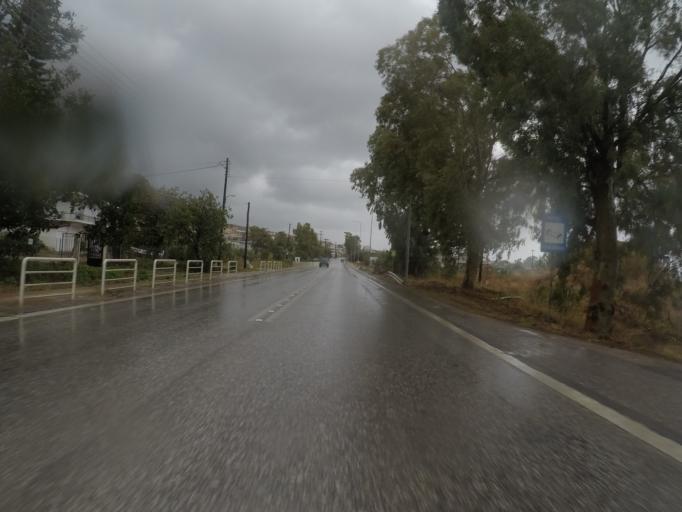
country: GR
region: Peloponnese
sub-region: Nomos Messinias
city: Kyparissia
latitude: 37.2552
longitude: 21.6790
